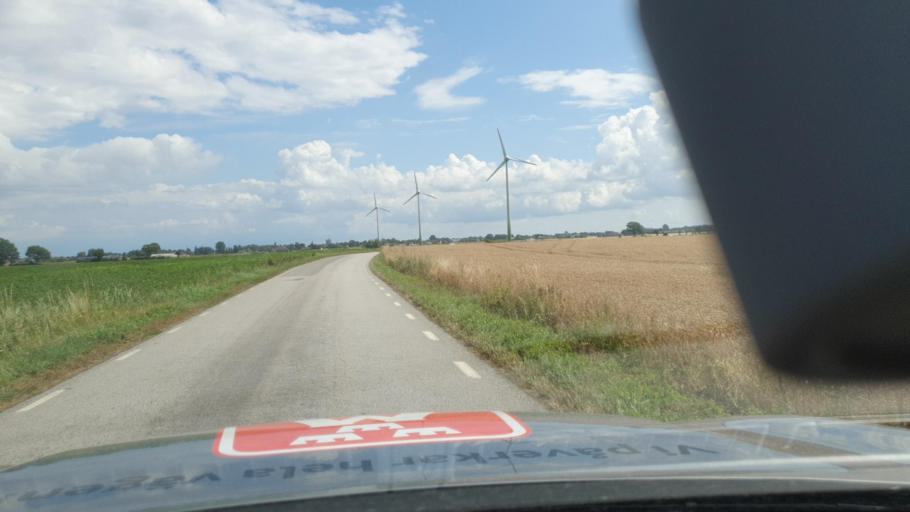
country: SE
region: Blekinge
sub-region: Solvesborgs Kommun
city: Soelvesborg
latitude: 56.0387
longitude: 14.6393
